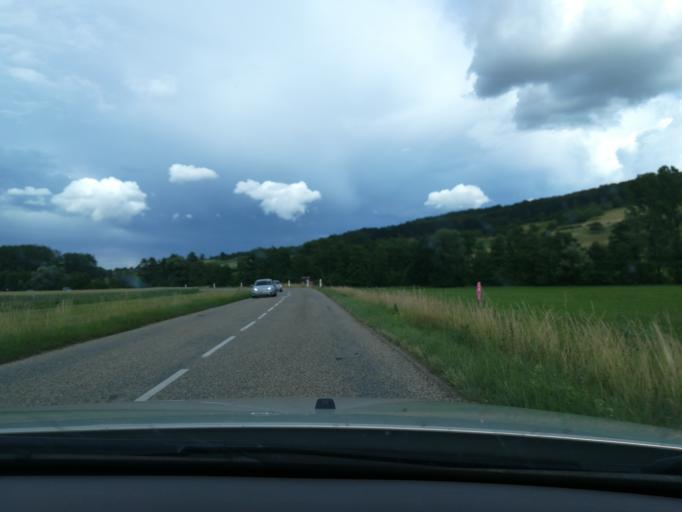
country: FR
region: Alsace
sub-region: Departement du Bas-Rhin
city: Neuwiller-les-Saverne
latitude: 48.8174
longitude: 7.4415
